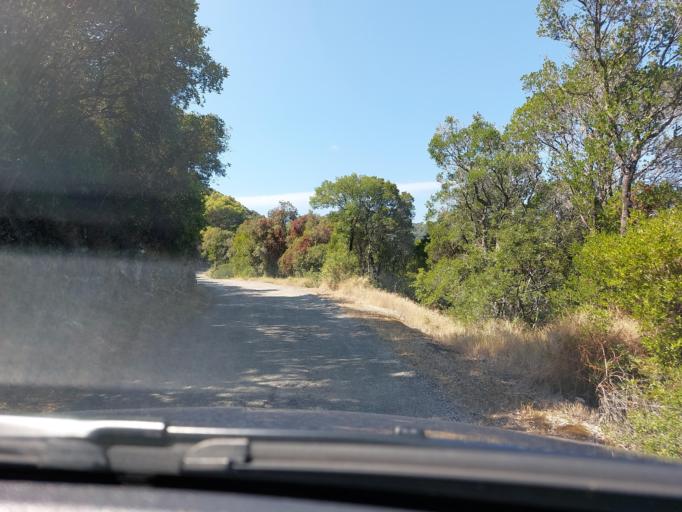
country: HR
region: Dubrovacko-Neretvanska
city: Smokvica
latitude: 42.7675
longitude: 16.8324
